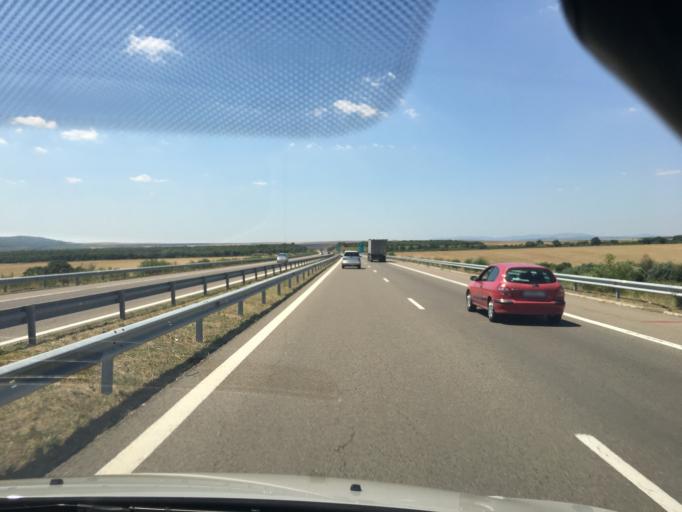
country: BG
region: Burgas
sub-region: Obshtina Karnobat
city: Karnobat
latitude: 42.5900
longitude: 27.0021
